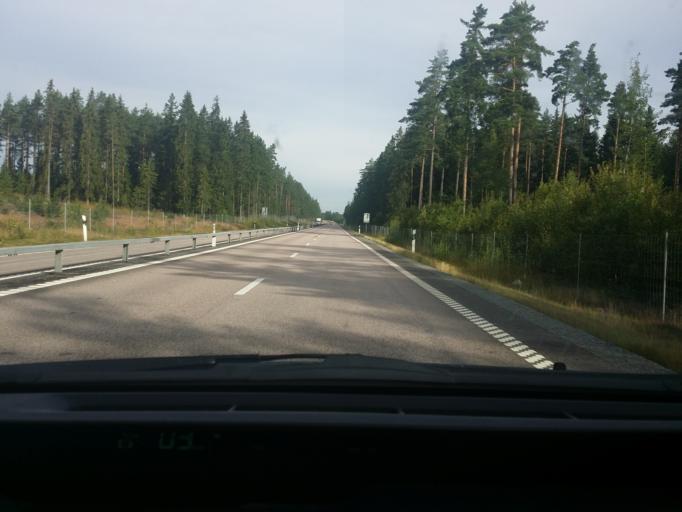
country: SE
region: Vaestmanland
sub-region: Sala Kommun
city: Sala
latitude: 59.8126
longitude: 16.5501
